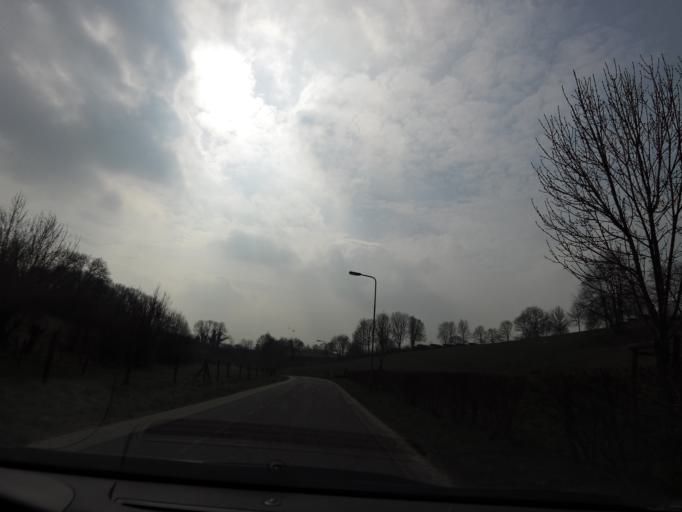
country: NL
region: Limburg
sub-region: Valkenburg aan de Geul
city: Schin op Geul
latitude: 50.8593
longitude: 5.8689
